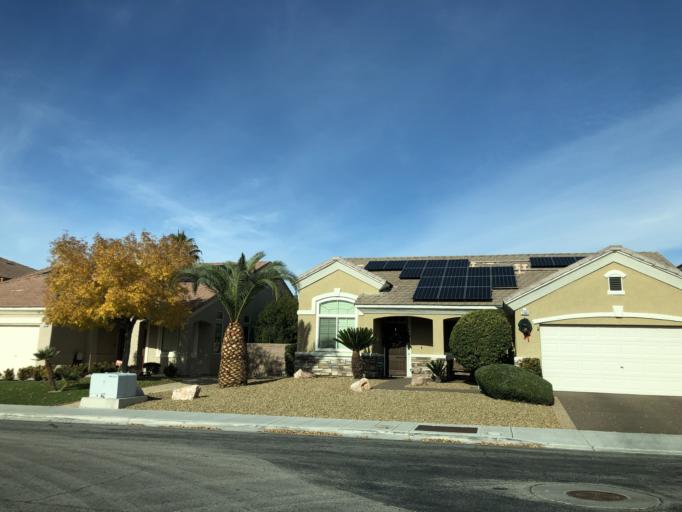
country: US
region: Nevada
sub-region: Clark County
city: Whitney
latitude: 36.0091
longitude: -115.0931
